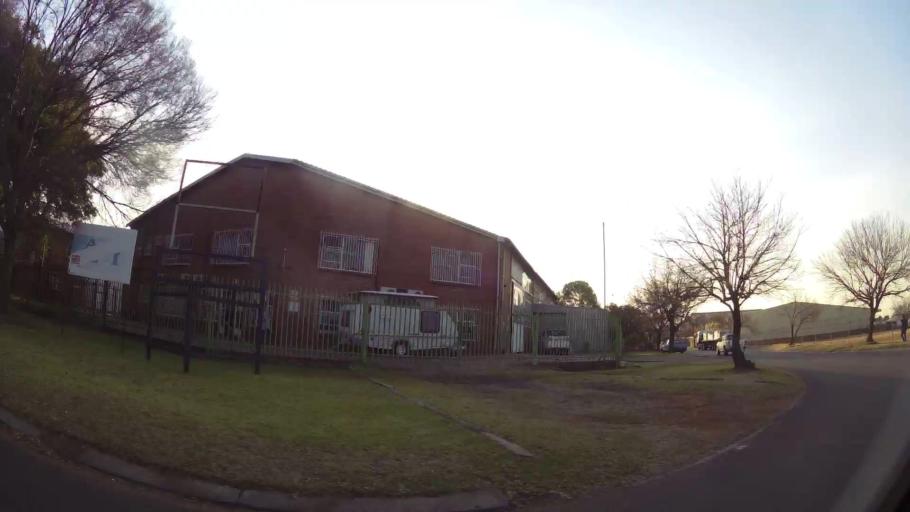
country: ZA
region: Gauteng
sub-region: Ekurhuleni Metropolitan Municipality
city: Springs
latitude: -26.2560
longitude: 28.4072
